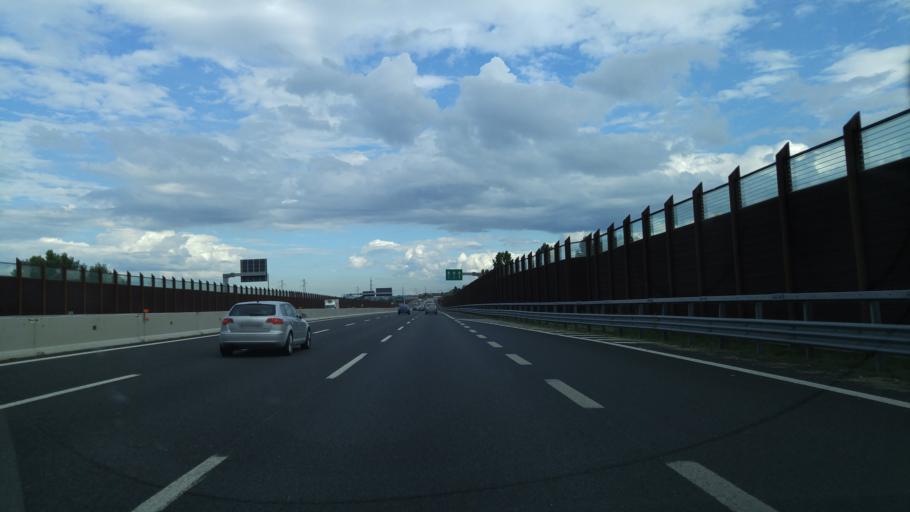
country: IT
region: Emilia-Romagna
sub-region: Provincia di Rimini
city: Rimini
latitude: 44.0334
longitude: 12.5719
